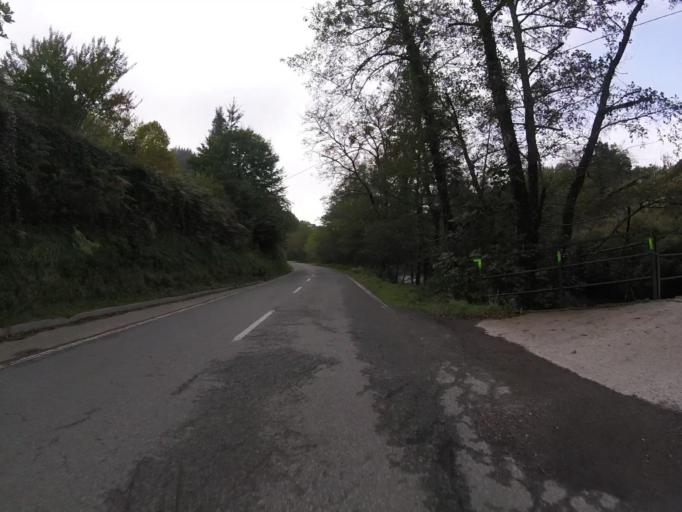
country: ES
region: Navarre
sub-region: Provincia de Navarra
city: Goizueta
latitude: 43.1887
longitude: -1.8571
